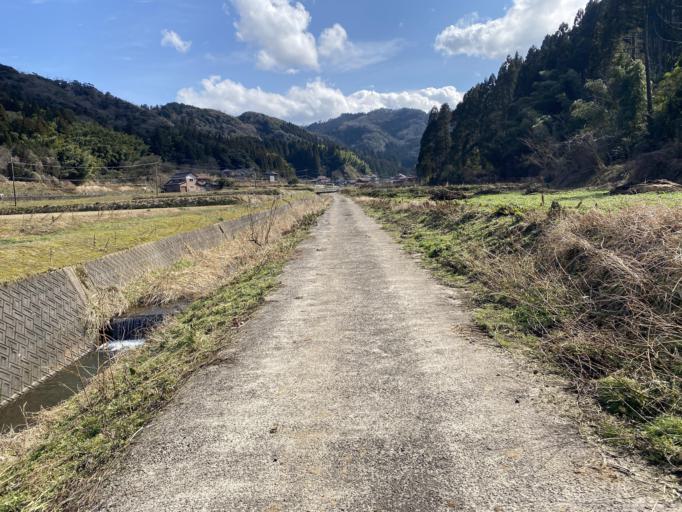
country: JP
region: Tottori
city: Kurayoshi
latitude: 35.4945
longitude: 133.9861
